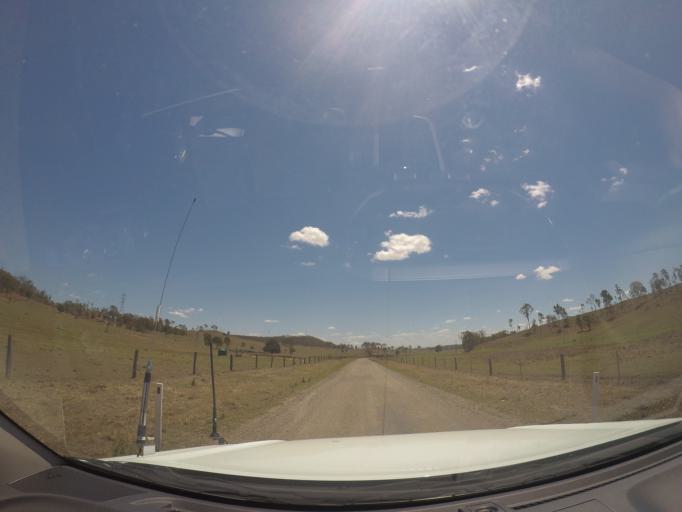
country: AU
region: Queensland
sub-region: Ipswich
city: Redbank Plains
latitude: -27.7485
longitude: 152.8311
